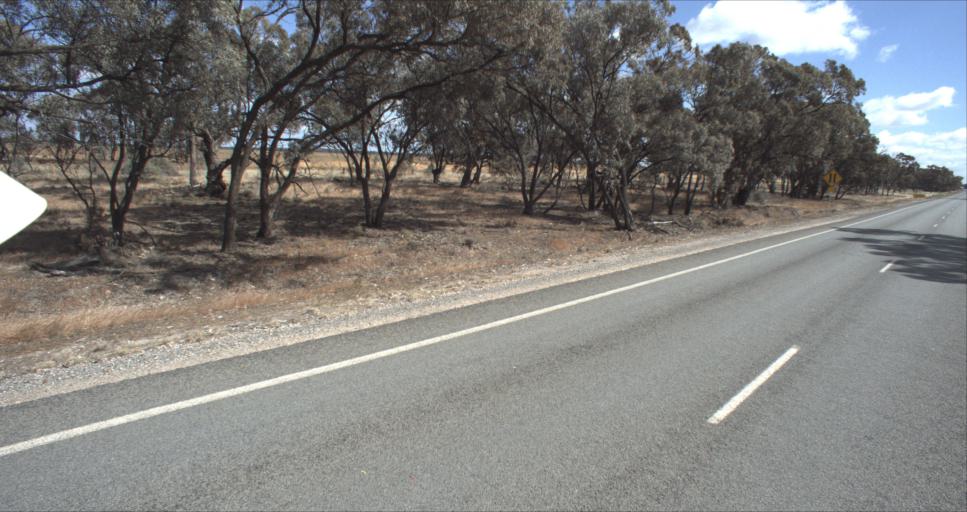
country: AU
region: New South Wales
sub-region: Murrumbidgee Shire
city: Darlington Point
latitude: -34.5636
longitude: 146.1686
